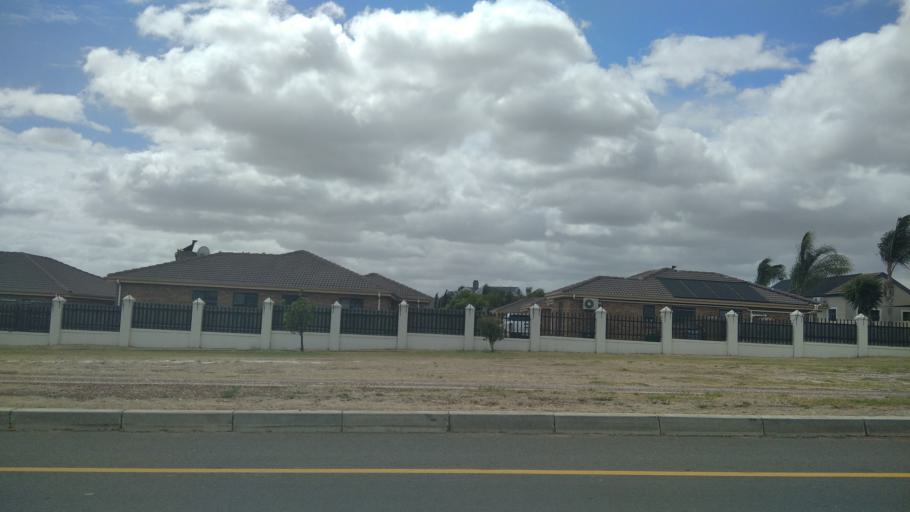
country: ZA
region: Western Cape
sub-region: City of Cape Town
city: Kraaifontein
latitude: -33.8181
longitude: 18.6763
